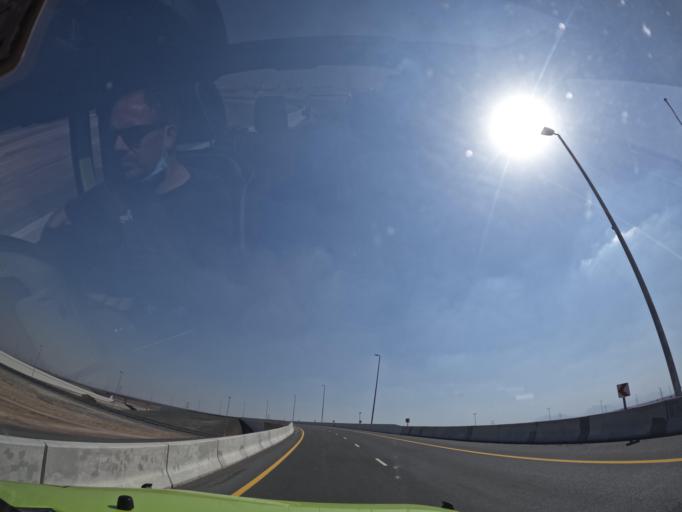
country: AE
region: Ash Shariqah
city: Adh Dhayd
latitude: 24.9081
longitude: 55.7996
